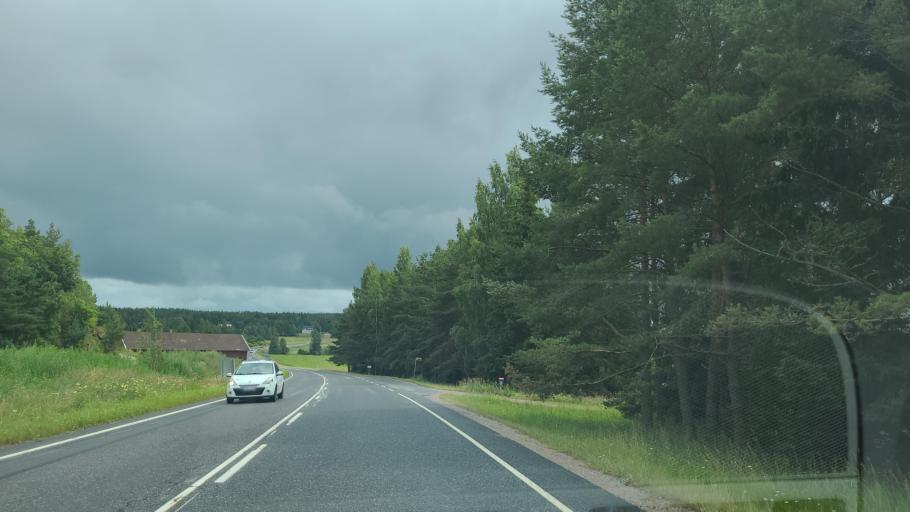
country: FI
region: Varsinais-Suomi
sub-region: Turku
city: Sauvo
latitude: 60.3353
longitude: 22.7046
